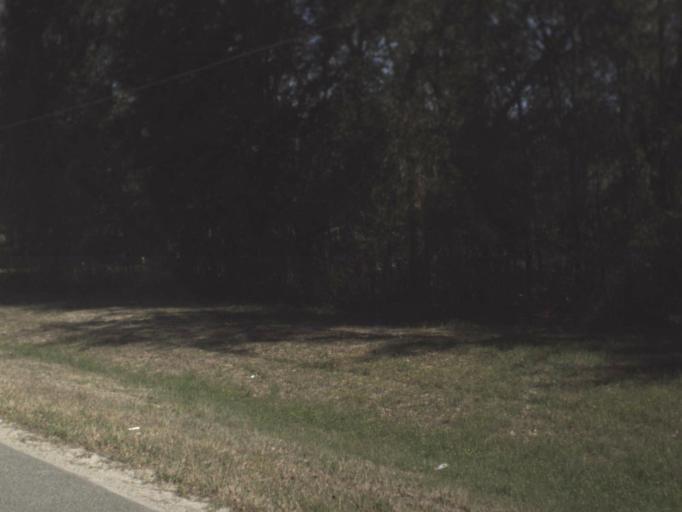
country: US
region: Florida
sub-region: Leon County
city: Woodville
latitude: 30.3287
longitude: -84.3114
